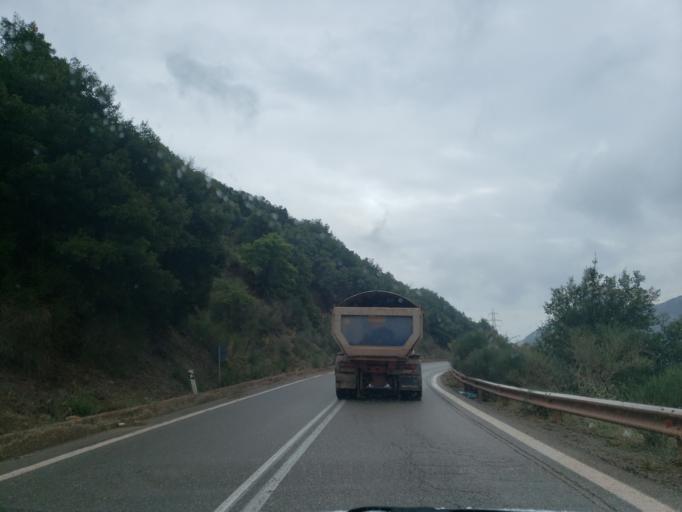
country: GR
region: Central Greece
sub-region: Nomos Fokidos
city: Amfissa
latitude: 38.5805
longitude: 22.3926
